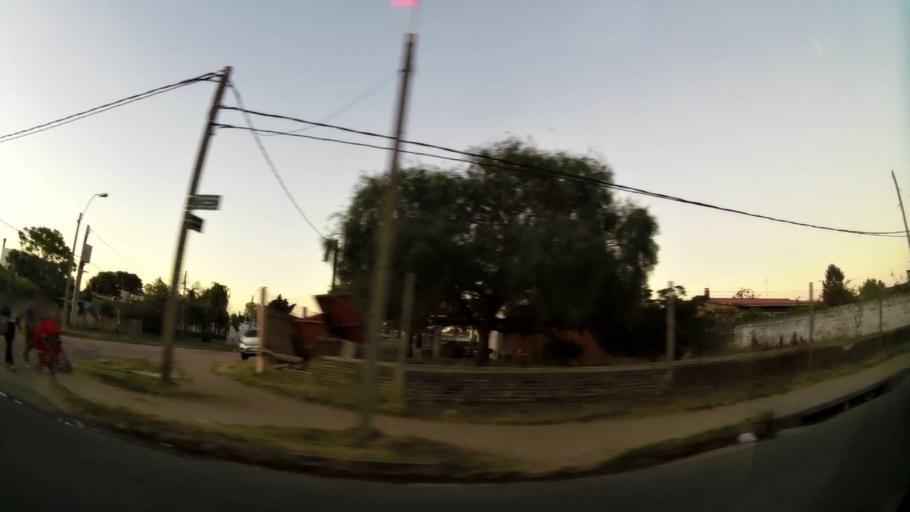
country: UY
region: Canelones
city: Toledo
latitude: -34.8176
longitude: -56.1470
